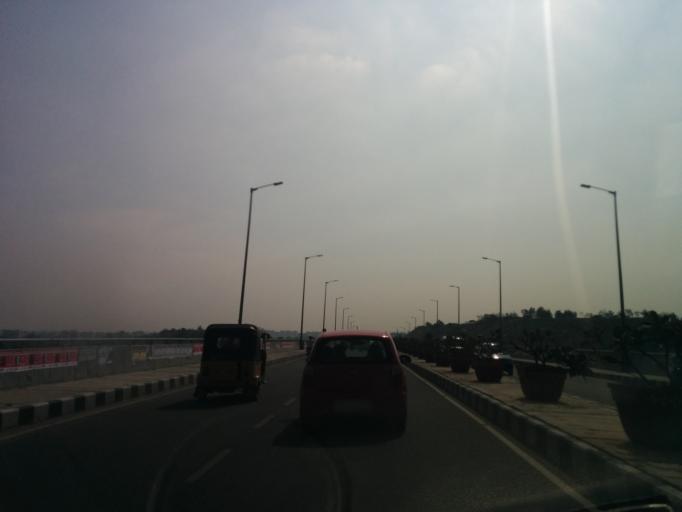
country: IN
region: Telangana
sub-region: Rangareddi
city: Kukatpalli
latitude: 17.4687
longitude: 78.3865
